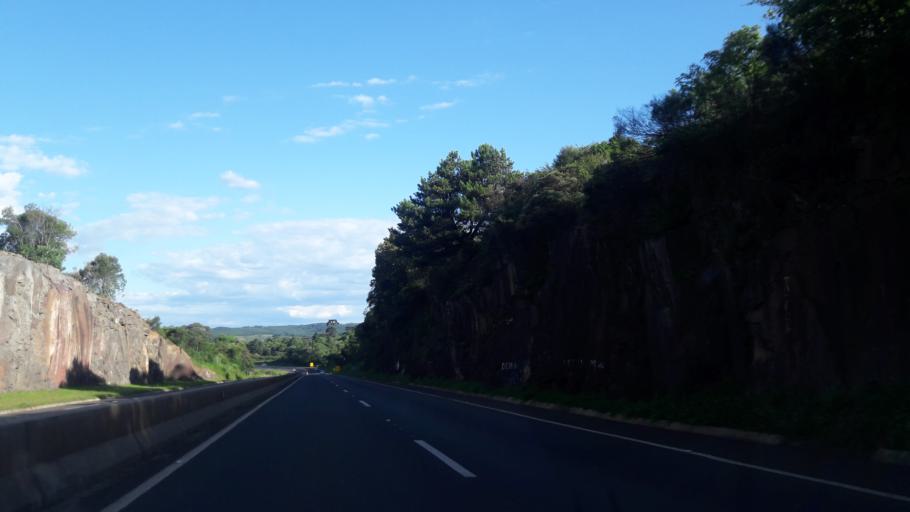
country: BR
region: Parana
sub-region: Guarapuava
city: Guarapuava
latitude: -25.3500
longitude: -51.3782
